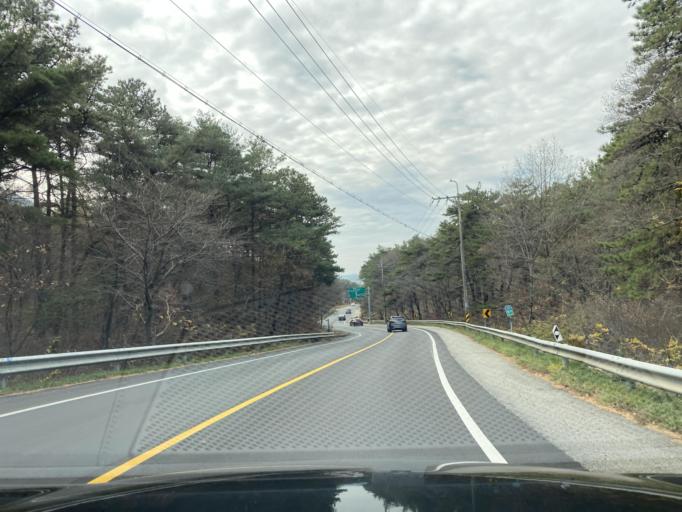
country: KR
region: Chungcheongnam-do
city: Hongsung
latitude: 36.6595
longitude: 126.6288
